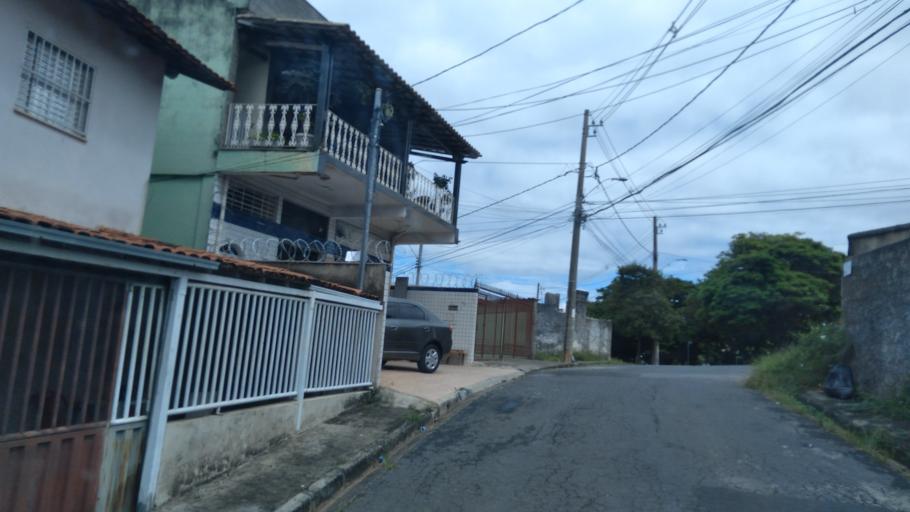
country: BR
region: Minas Gerais
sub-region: Belo Horizonte
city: Belo Horizonte
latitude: -19.8674
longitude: -43.9094
